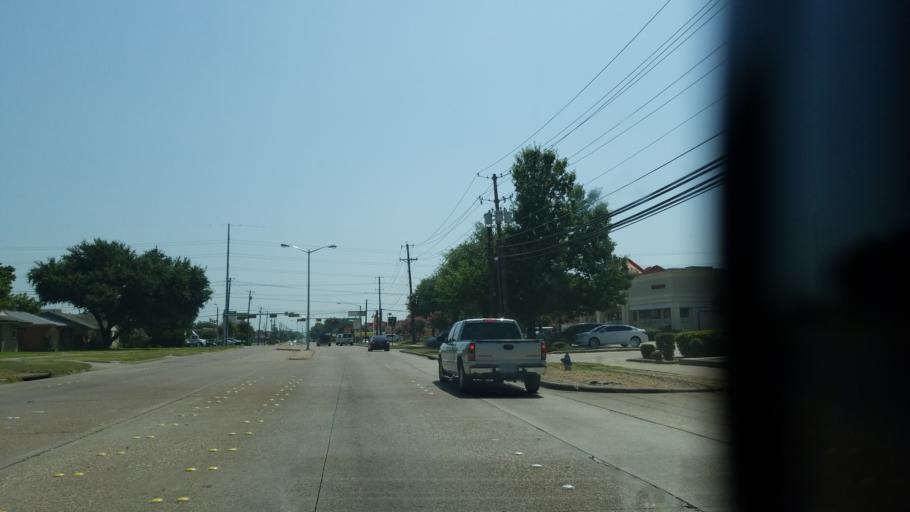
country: US
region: Texas
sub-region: Dallas County
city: Garland
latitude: 32.9164
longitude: -96.6669
